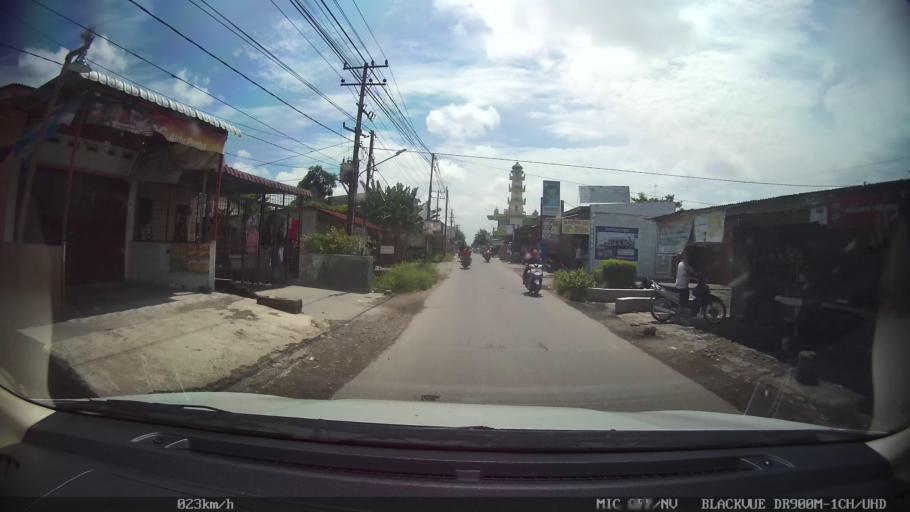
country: ID
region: North Sumatra
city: Medan
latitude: 3.6020
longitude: 98.7627
